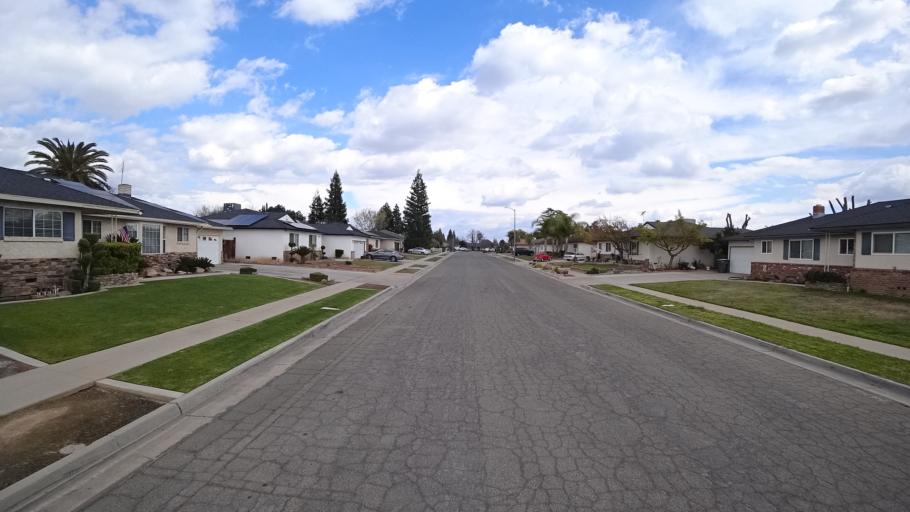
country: US
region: California
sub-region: Fresno County
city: Clovis
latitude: 36.8331
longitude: -119.7711
